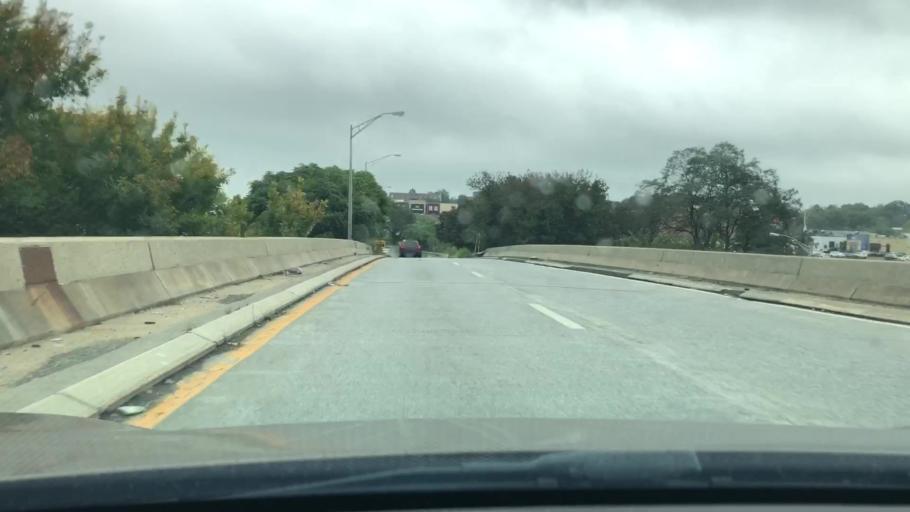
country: US
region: New York
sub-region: Westchester County
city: Bronxville
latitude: 40.9307
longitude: -73.8553
